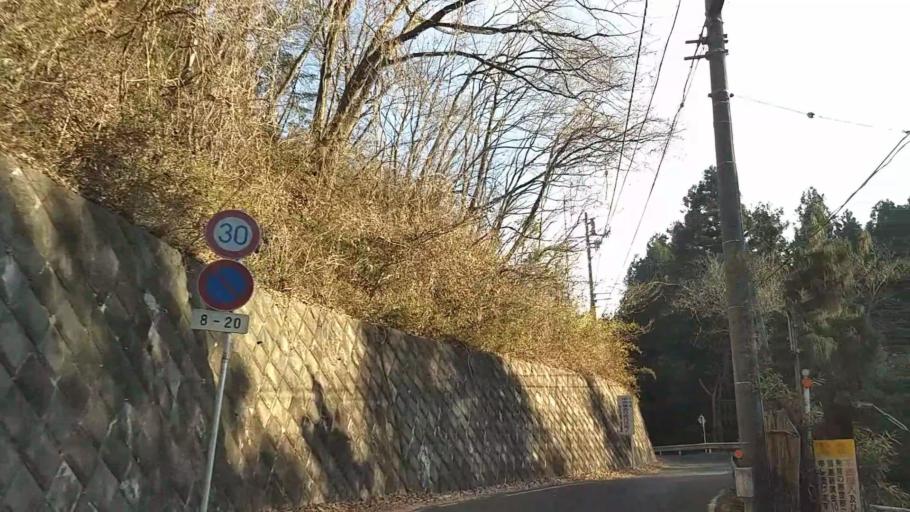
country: JP
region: Yamanashi
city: Uenohara
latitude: 35.5599
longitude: 139.2068
